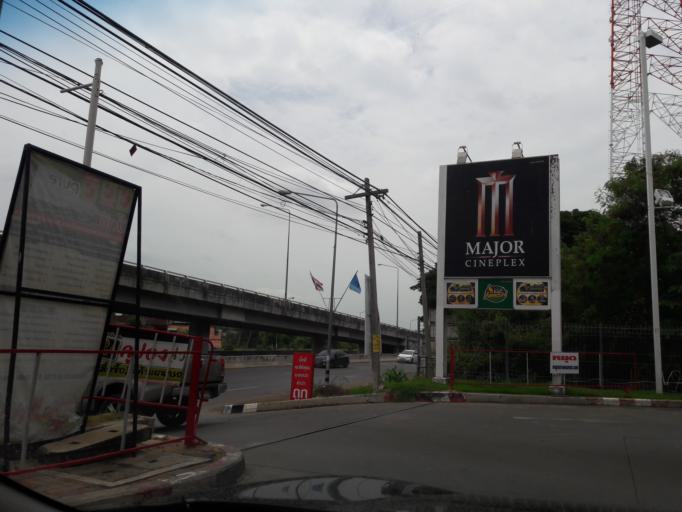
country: TH
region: Ratchaburi
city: Ratchaburi
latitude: 13.5503
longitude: 99.8239
